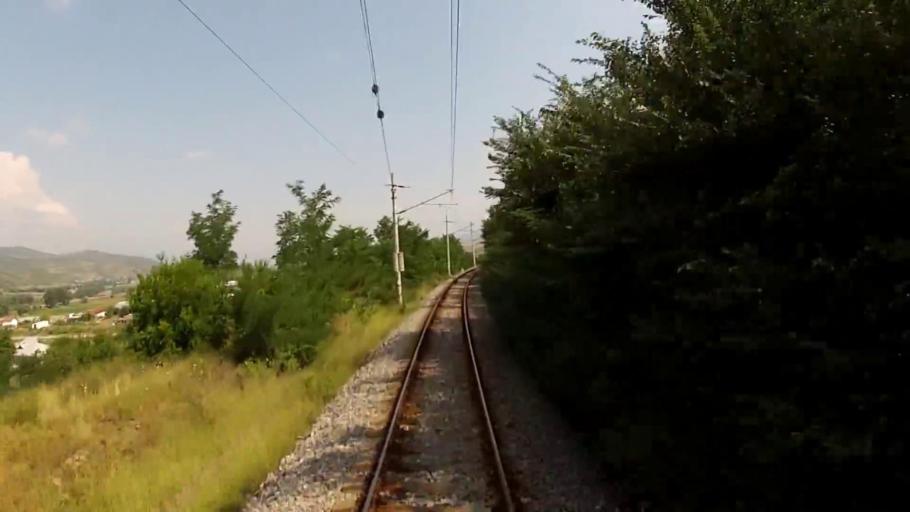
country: BG
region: Blagoevgrad
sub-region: Obshtina Sandanski
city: Sandanski
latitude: 41.5700
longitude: 23.2422
